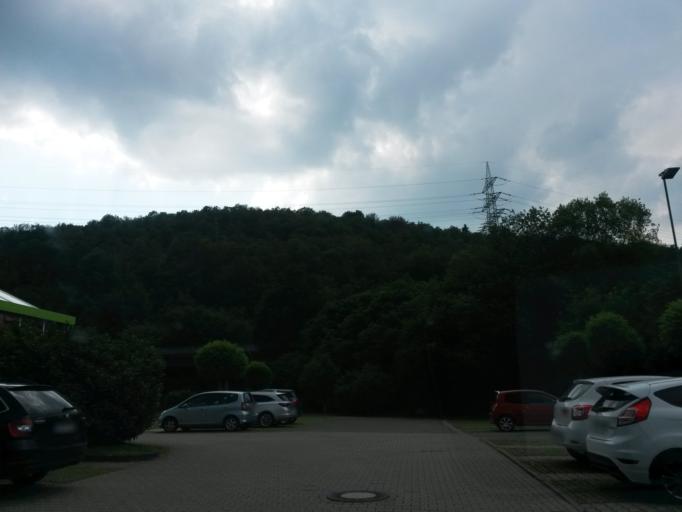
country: DE
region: North Rhine-Westphalia
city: Kreuztal
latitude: 50.9391
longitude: 7.9997
